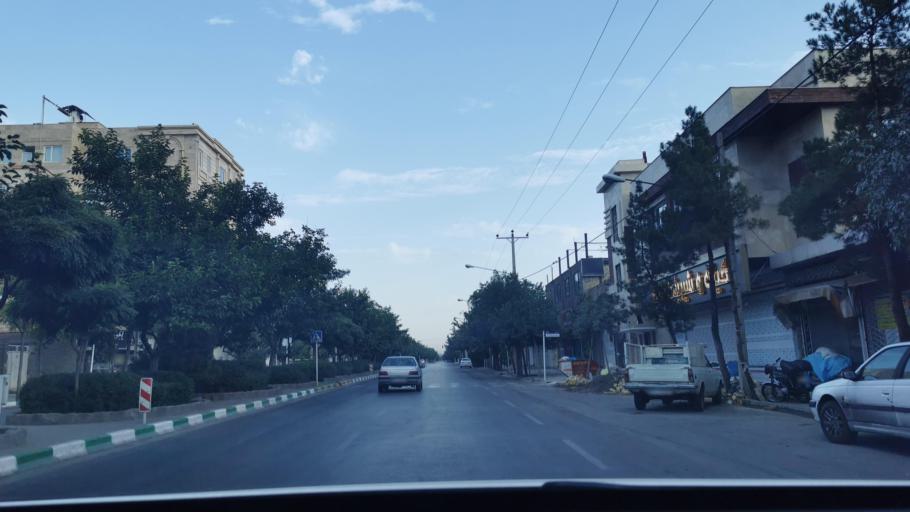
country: IR
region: Razavi Khorasan
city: Mashhad
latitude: 36.3590
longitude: 59.5241
